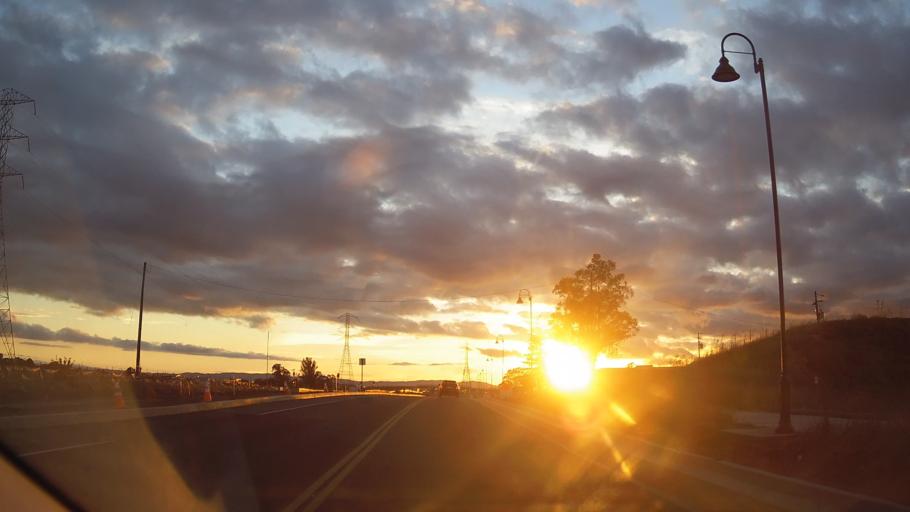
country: US
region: California
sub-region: Solano County
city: Vacaville
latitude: 38.2905
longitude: -121.9596
